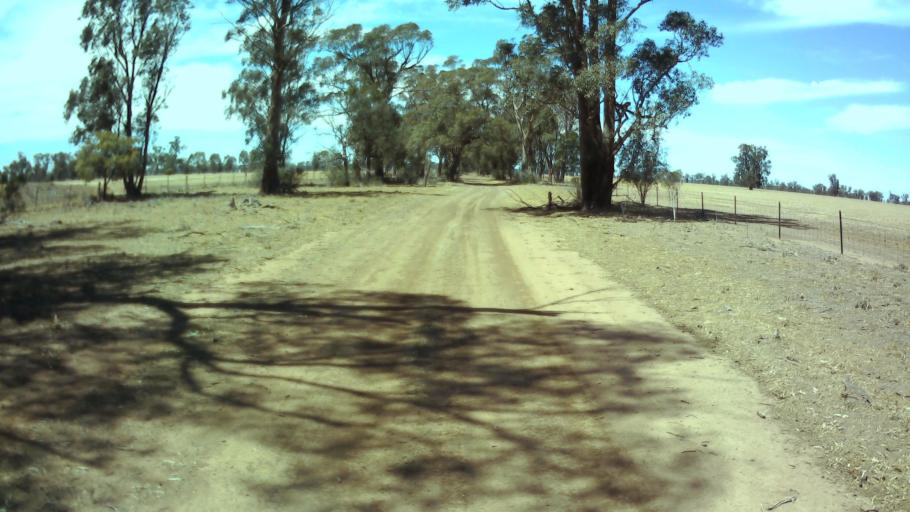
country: AU
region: New South Wales
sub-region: Weddin
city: Grenfell
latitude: -33.9189
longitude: 147.8050
